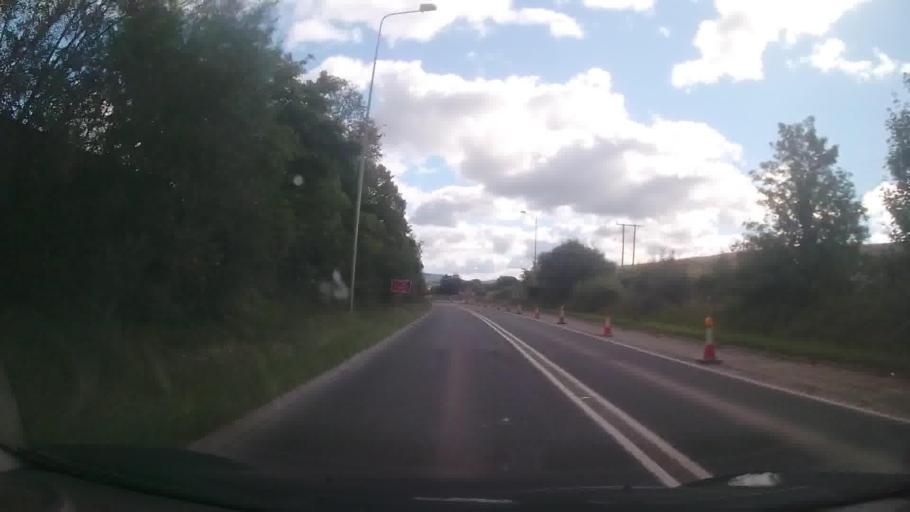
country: GB
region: Wales
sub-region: Rhondda Cynon Taf
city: Hirwaun
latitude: 51.7354
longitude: -3.5098
